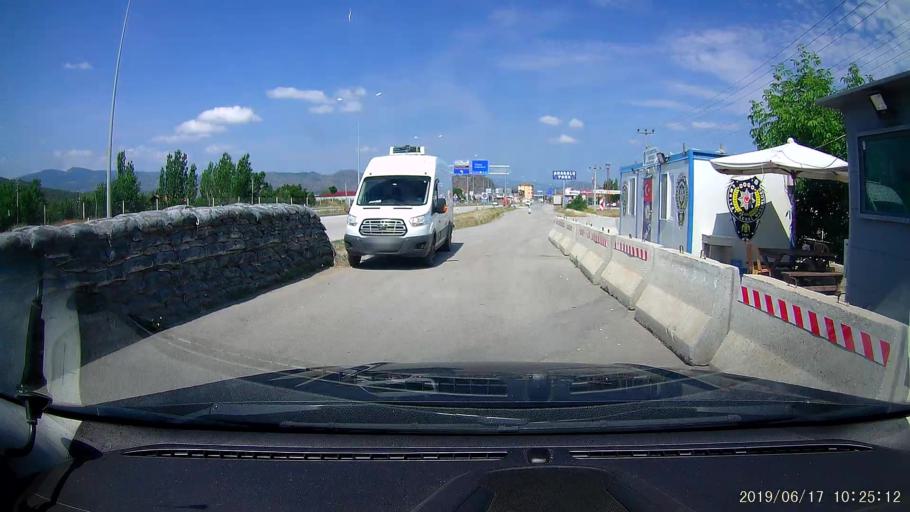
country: TR
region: Corum
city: Osmancik
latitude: 40.9709
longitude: 34.8274
